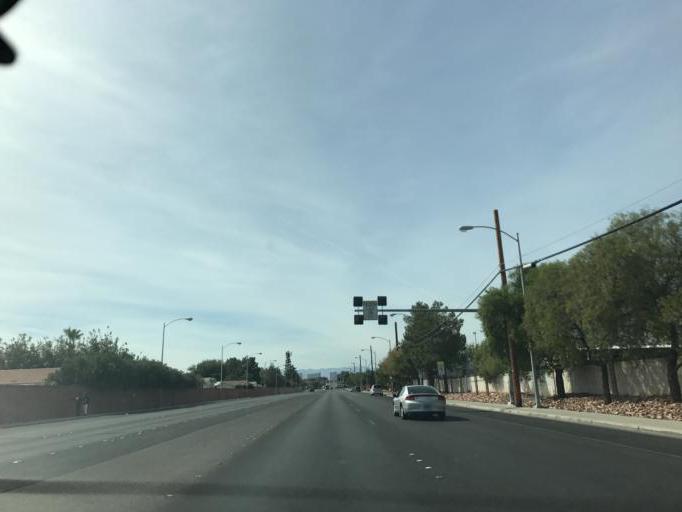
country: US
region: Nevada
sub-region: Clark County
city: Winchester
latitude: 36.1297
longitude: -115.0598
